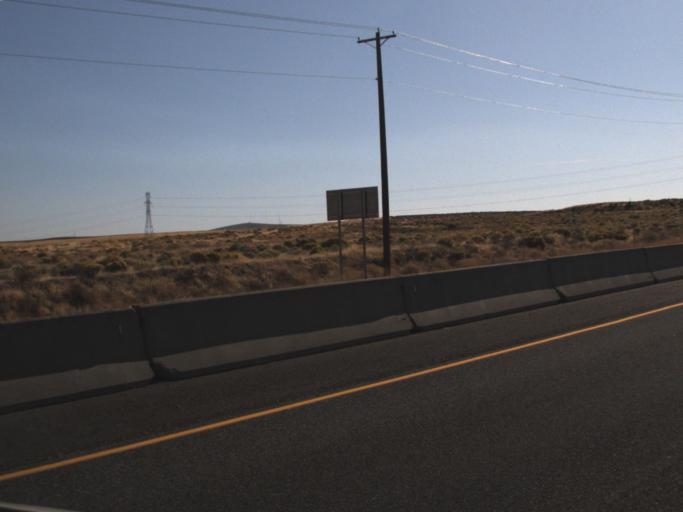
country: US
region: Washington
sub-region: Benton County
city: Kennewick
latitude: 46.1753
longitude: -119.1895
